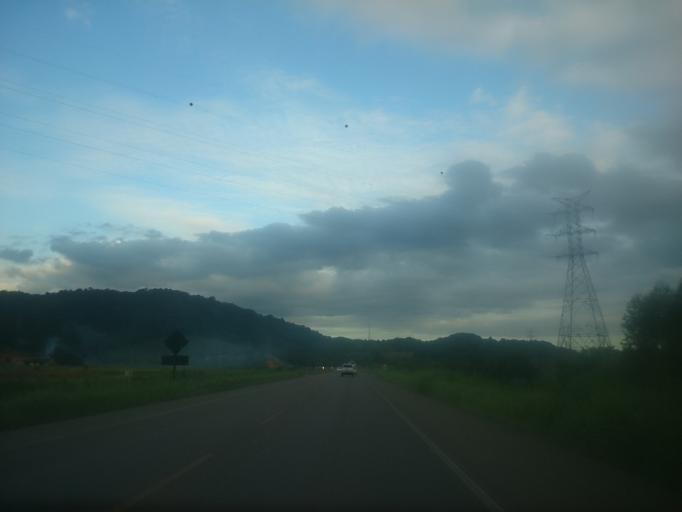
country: BR
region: Santa Catarina
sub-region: Blumenau
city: Blumenau
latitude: -26.8691
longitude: -49.0266
